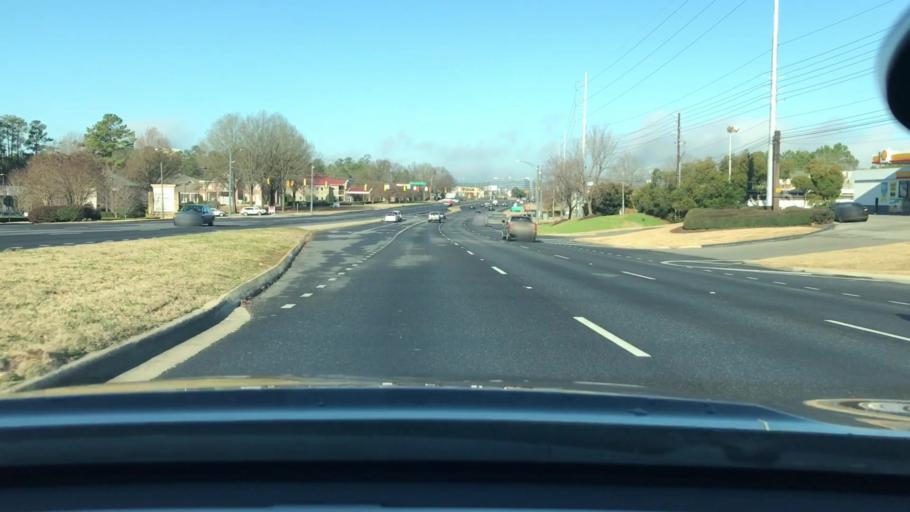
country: US
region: Alabama
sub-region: Shelby County
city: Lake Purdy
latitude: 33.4222
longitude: -86.6989
